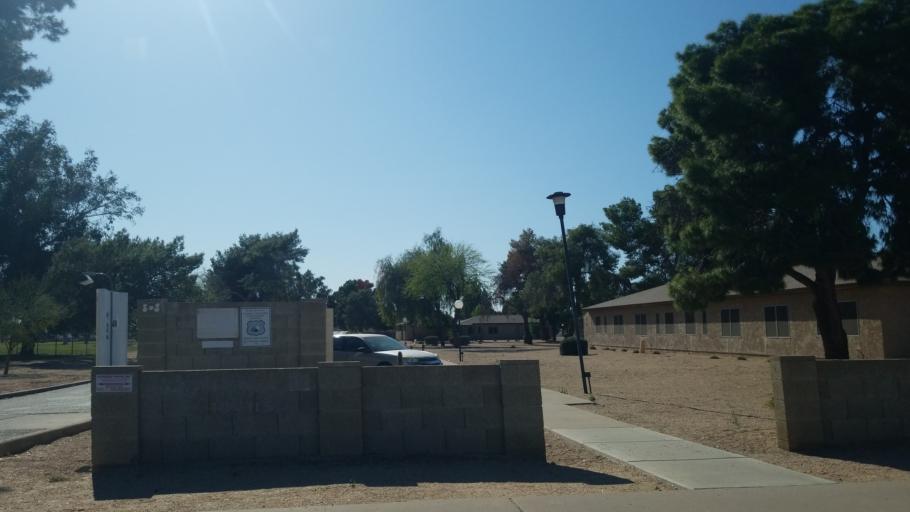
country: US
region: Arizona
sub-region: Maricopa County
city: Glendale
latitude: 33.5583
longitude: -112.1734
